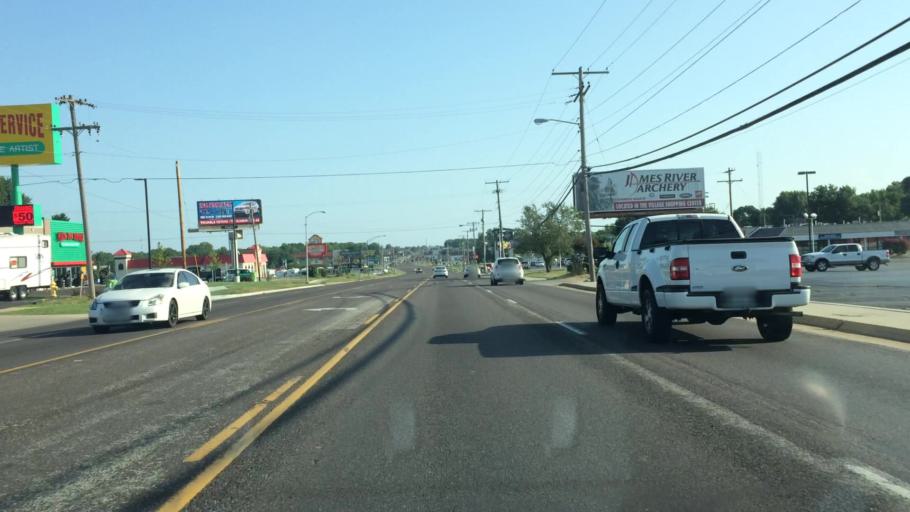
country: US
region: Missouri
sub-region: Greene County
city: Springfield
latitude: 37.1621
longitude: -93.2954
